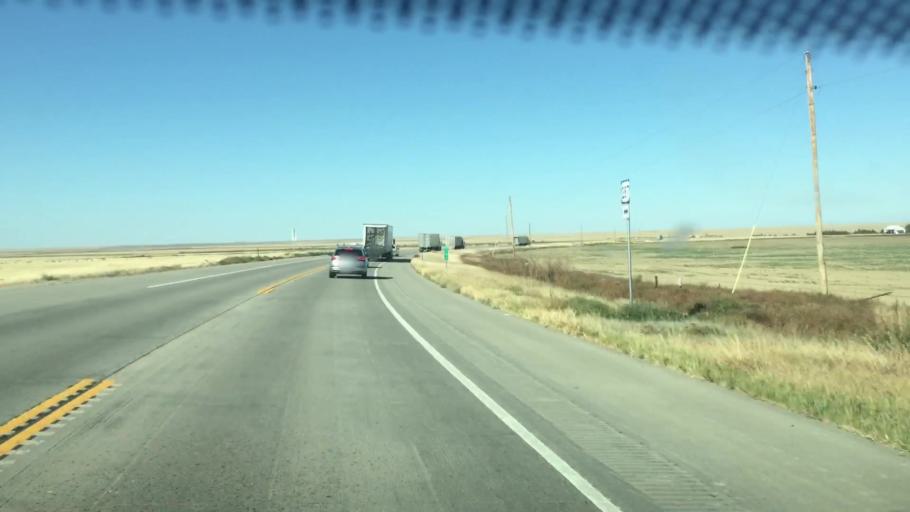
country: US
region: Colorado
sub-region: Kiowa County
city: Eads
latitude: 38.3389
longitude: -102.7200
